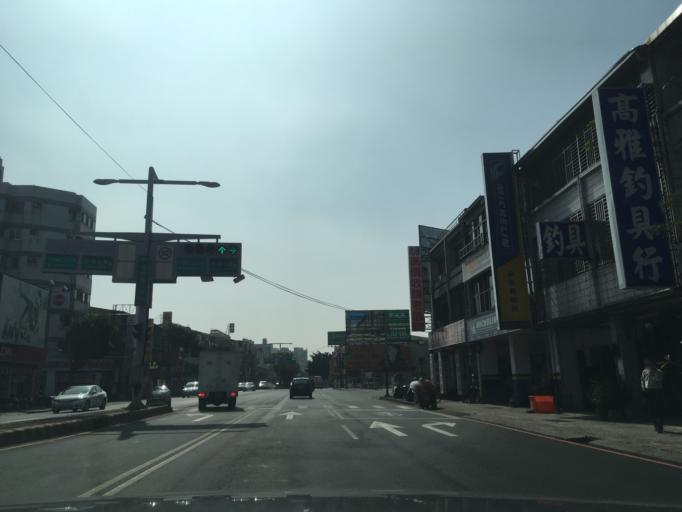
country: TW
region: Taiwan
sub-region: Taichung City
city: Taichung
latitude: 24.1937
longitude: 120.6593
